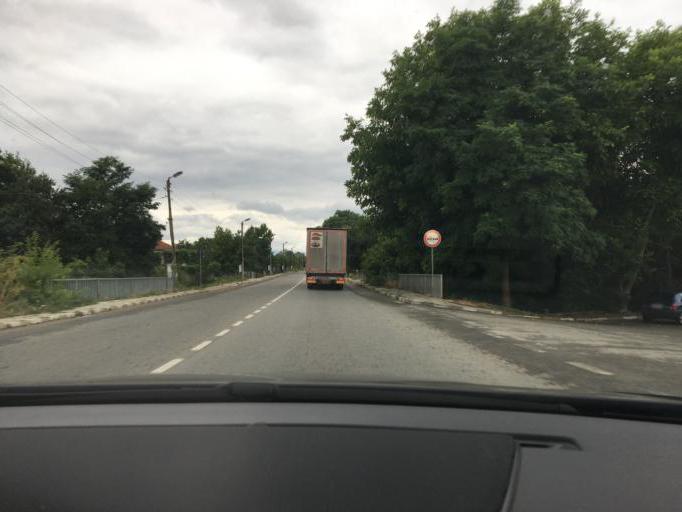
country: BG
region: Kyustendil
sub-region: Obshtina Kyustendil
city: Kyustendil
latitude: 42.2674
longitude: 22.8054
